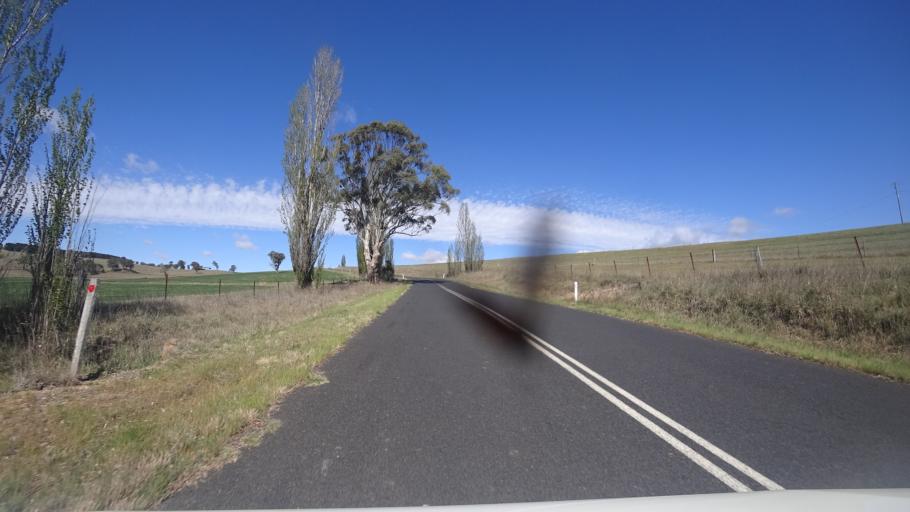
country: AU
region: New South Wales
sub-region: Lithgow
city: Portland
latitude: -33.5171
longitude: 149.9539
